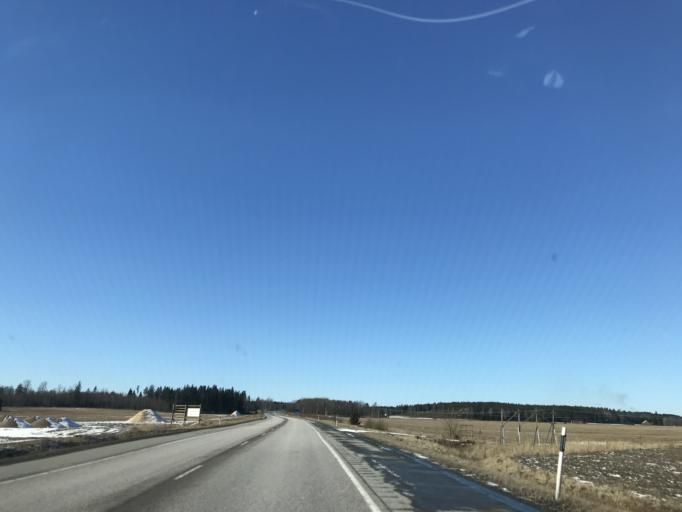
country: FI
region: Uusimaa
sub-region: Raaseporin
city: Inga
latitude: 60.0506
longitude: 23.9592
